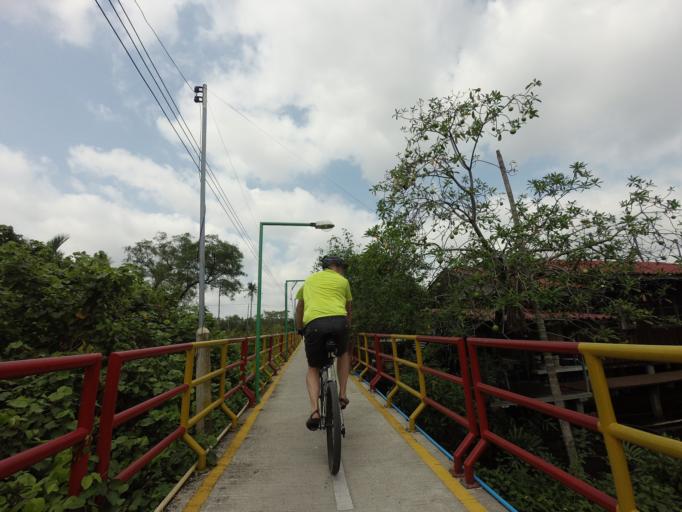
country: TH
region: Samut Prakan
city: Phra Pradaeng
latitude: 13.6652
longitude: 100.5618
